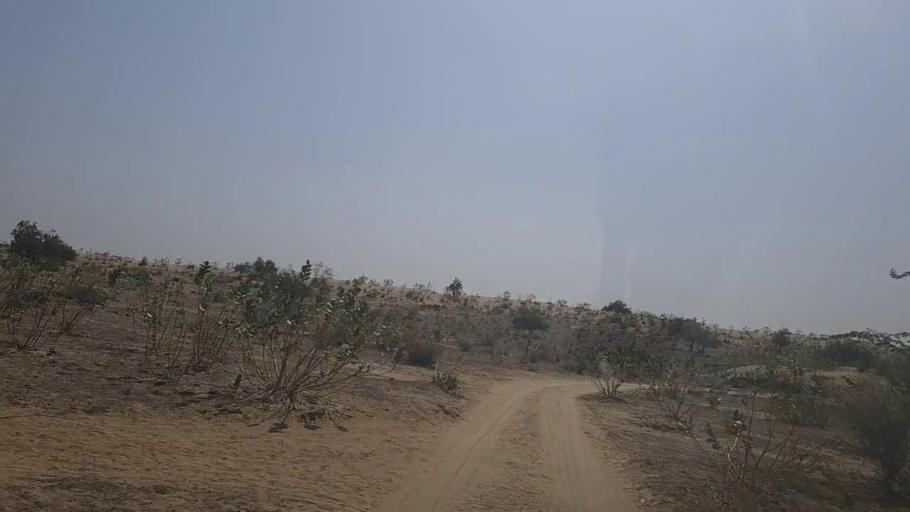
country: PK
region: Sindh
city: Naukot
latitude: 24.8202
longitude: 69.4798
